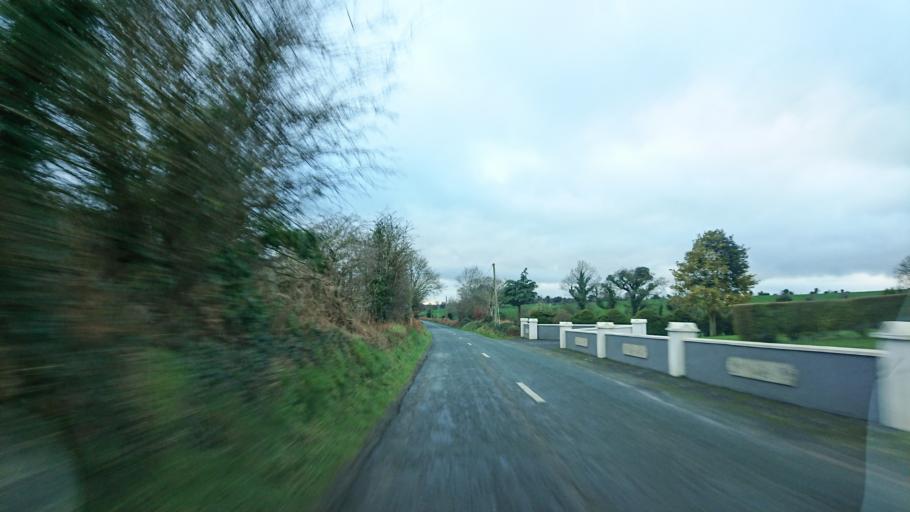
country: IE
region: Munster
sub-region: Waterford
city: Portlaw
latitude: 52.2233
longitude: -7.4120
